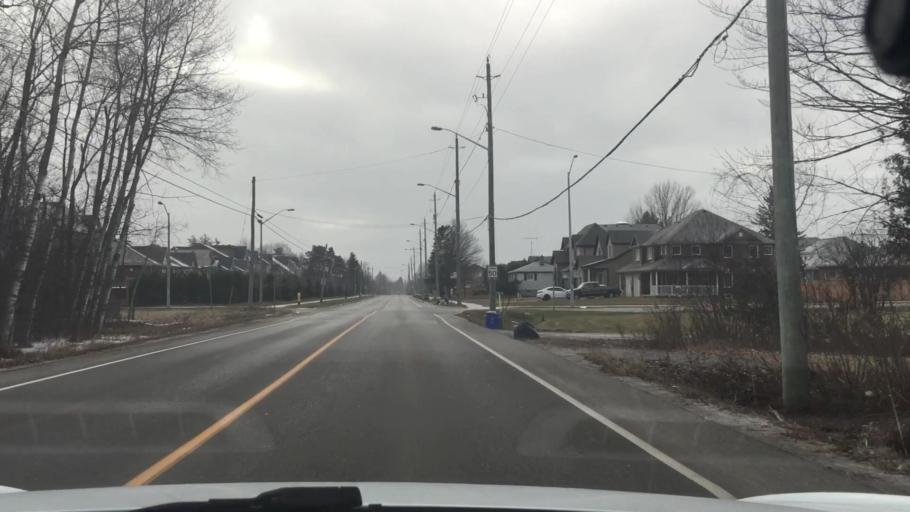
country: CA
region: Ontario
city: Oshawa
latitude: 43.9234
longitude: -78.7940
